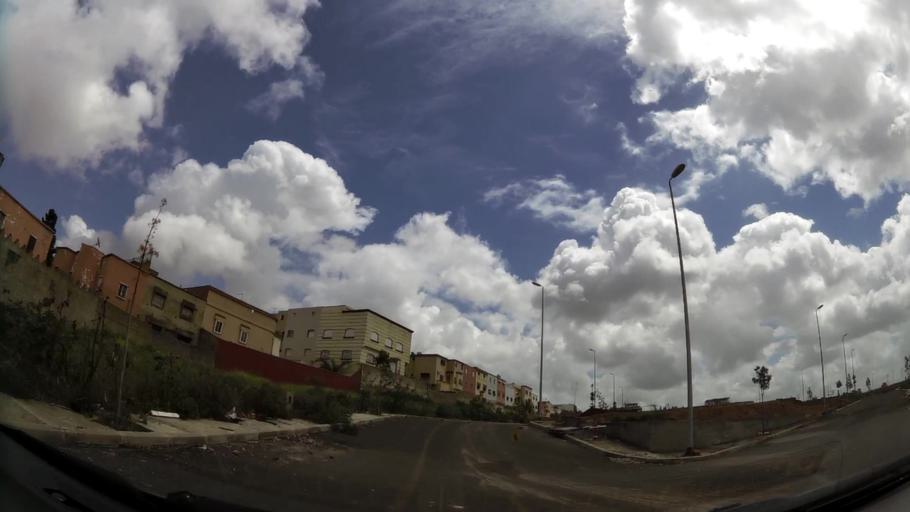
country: MA
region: Grand Casablanca
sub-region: Casablanca
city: Casablanca
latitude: 33.5312
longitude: -7.6040
